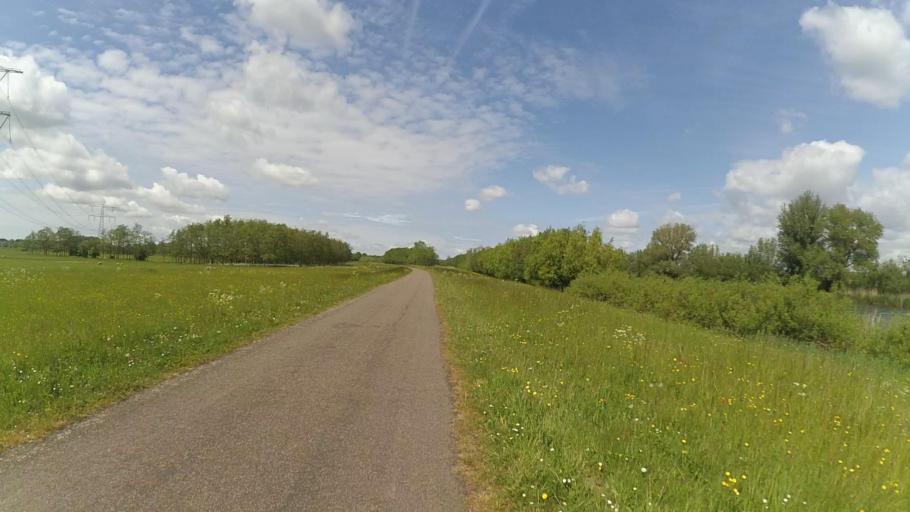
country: NL
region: South Holland
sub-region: Gemeente Spijkenisse
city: Spijkenisse
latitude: 51.8411
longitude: 4.2608
